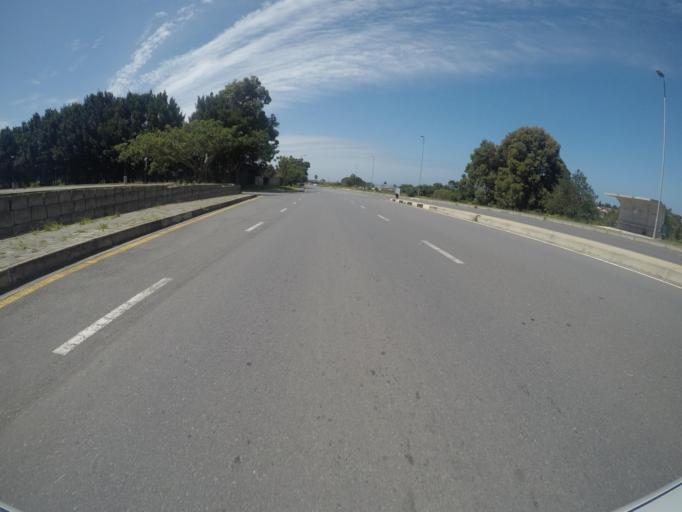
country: ZA
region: Eastern Cape
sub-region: Buffalo City Metropolitan Municipality
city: East London
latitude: -32.9372
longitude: 27.9934
